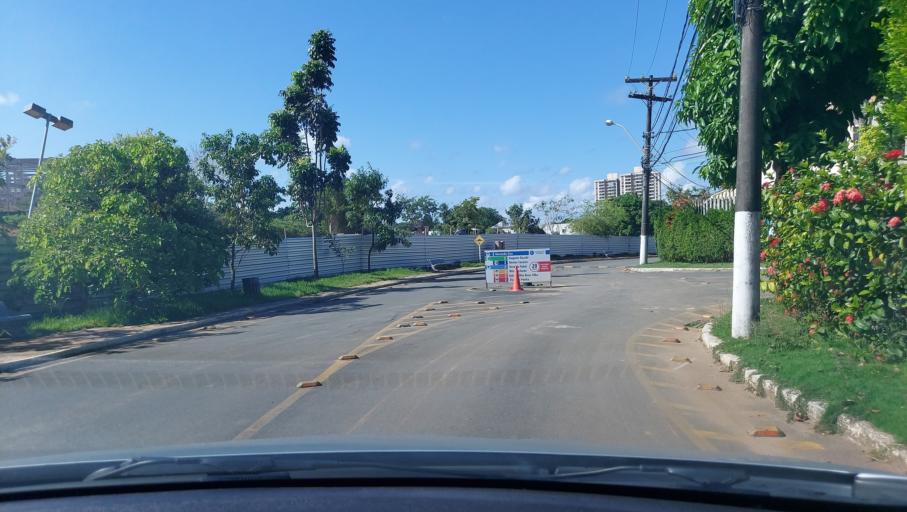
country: BR
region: Bahia
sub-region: Lauro De Freitas
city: Lauro de Freitas
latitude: -12.9436
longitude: -38.3843
